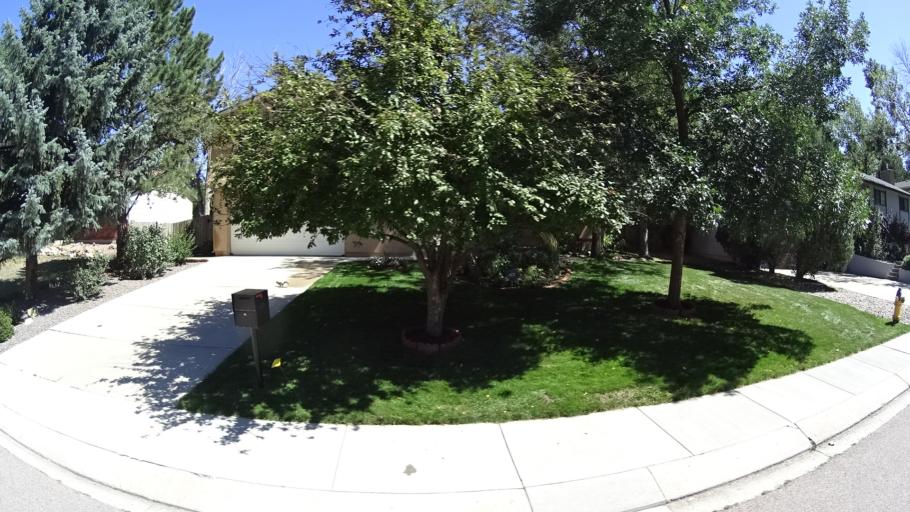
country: US
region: Colorado
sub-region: El Paso County
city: Air Force Academy
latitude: 38.9245
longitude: -104.8046
